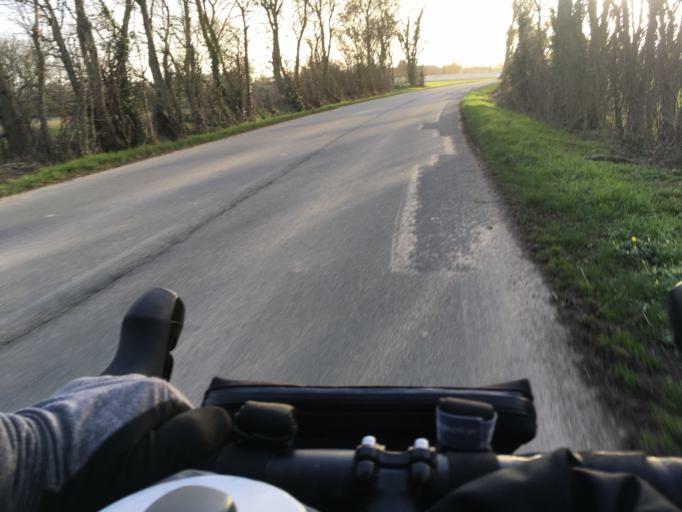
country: FR
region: Poitou-Charentes
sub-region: Departement de la Charente-Maritime
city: Courcon
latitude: 46.1667
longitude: -0.8536
